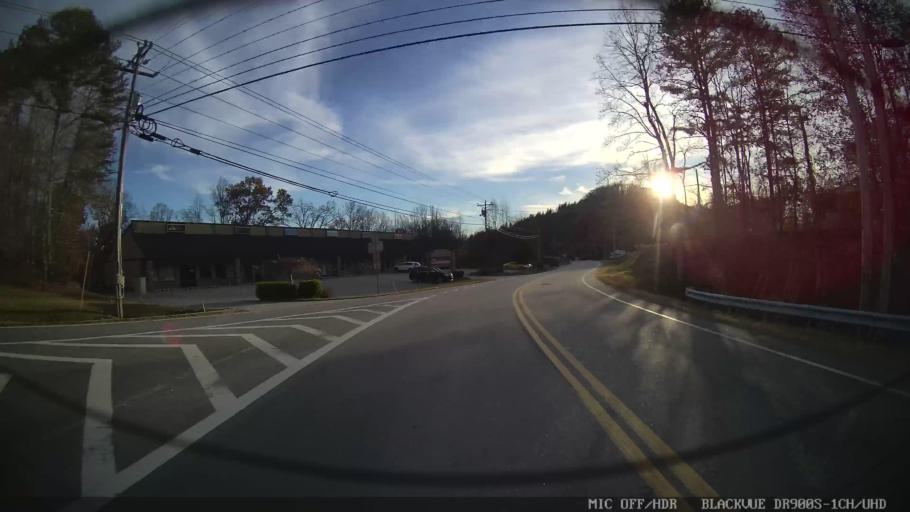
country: US
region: Georgia
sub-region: Union County
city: Blairsville
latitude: 34.8723
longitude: -83.9478
